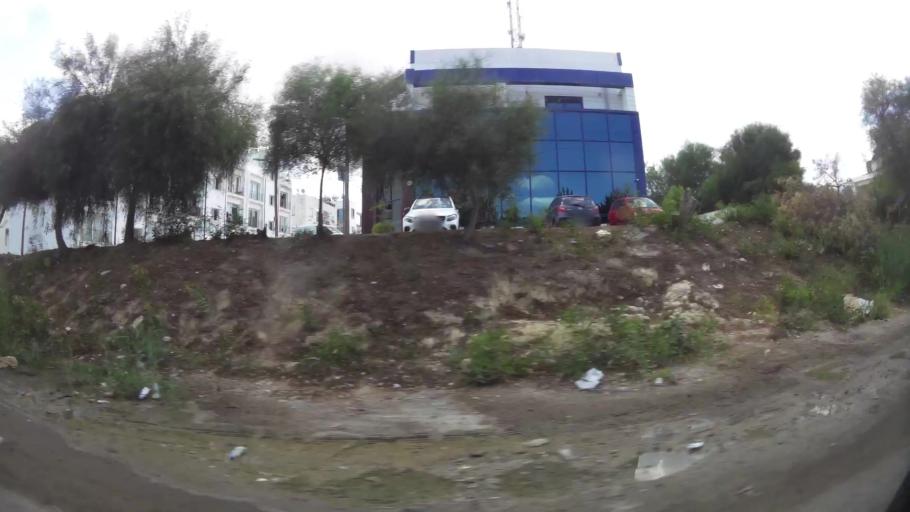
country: CY
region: Lefkosia
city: Nicosia
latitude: 35.2099
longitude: 33.3636
